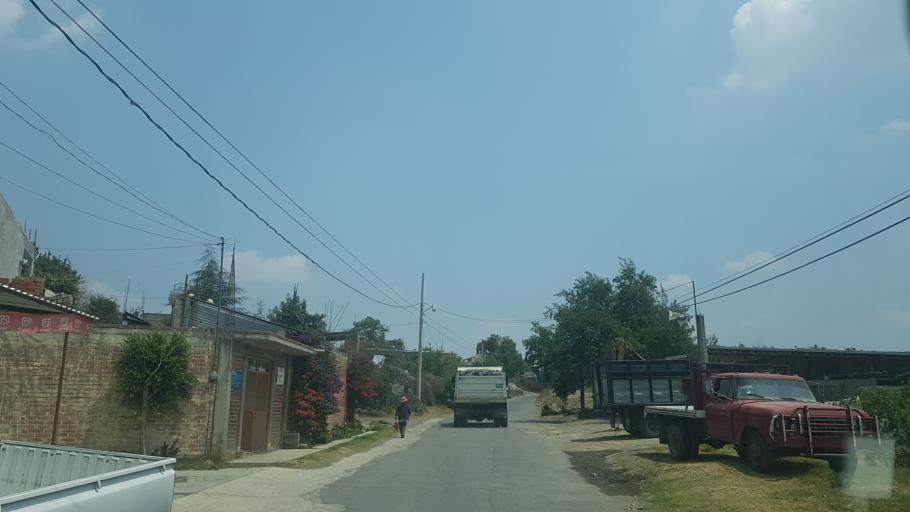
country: MX
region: Puebla
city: San Andres Calpan
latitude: 19.1002
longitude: -98.4752
